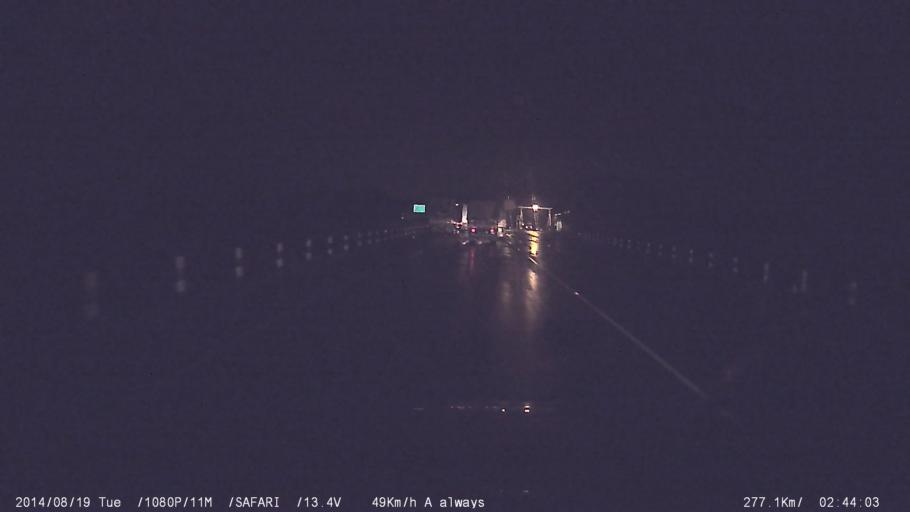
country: IN
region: Tamil Nadu
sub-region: Coimbatore
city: Irugur
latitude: 11.0113
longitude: 77.0726
